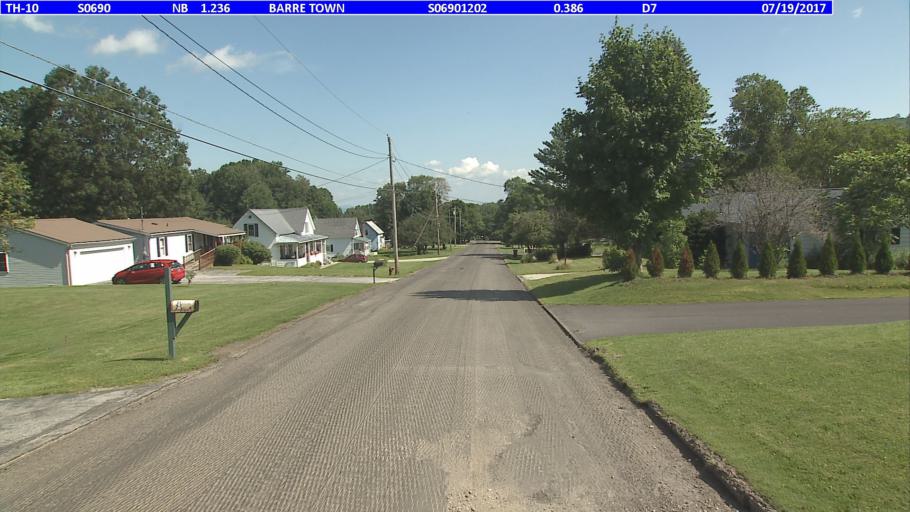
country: US
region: Vermont
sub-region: Washington County
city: South Barre
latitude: 44.1493
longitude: -72.4930
